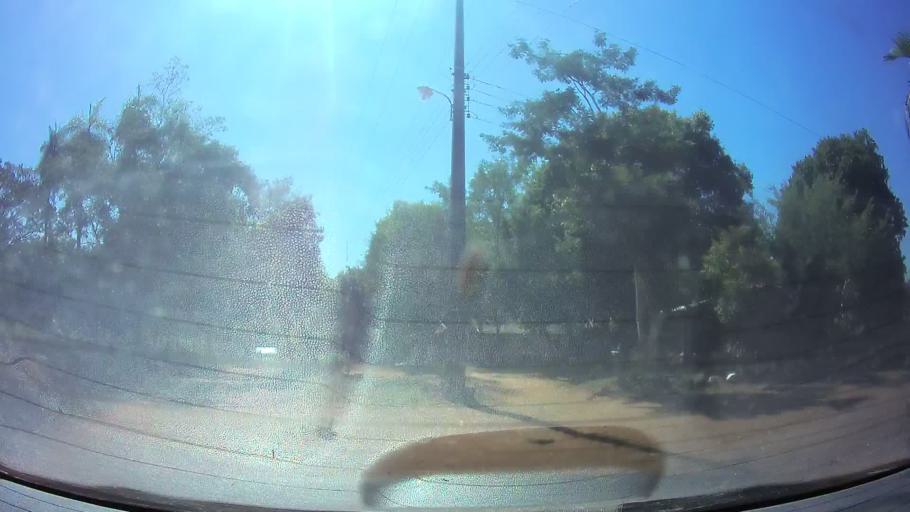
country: PY
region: Central
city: Limpio
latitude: -25.2440
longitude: -57.4471
